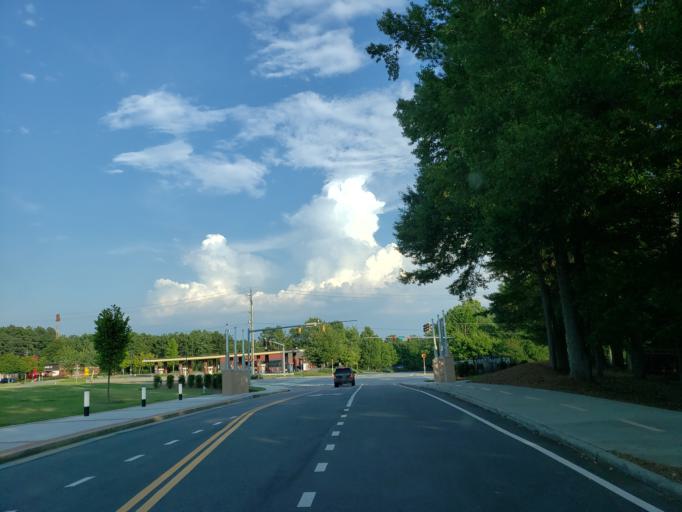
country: US
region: Georgia
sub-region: Cobb County
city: Kennesaw
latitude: 34.0326
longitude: -84.5819
